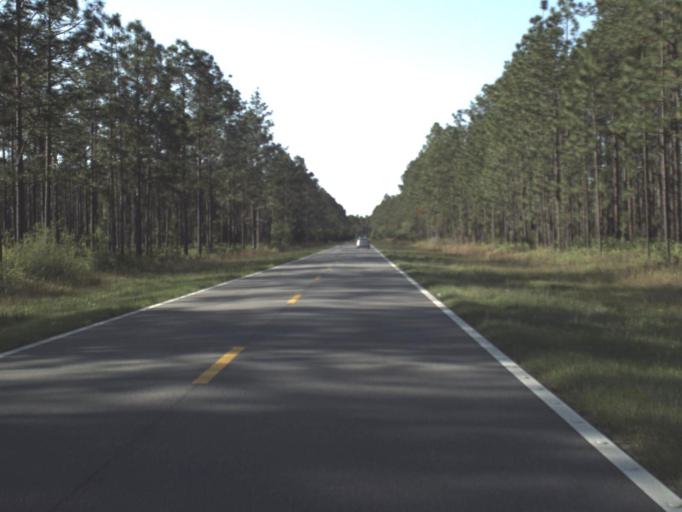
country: US
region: Florida
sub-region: Gulf County
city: Wewahitchka
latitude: 30.1212
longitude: -84.9885
